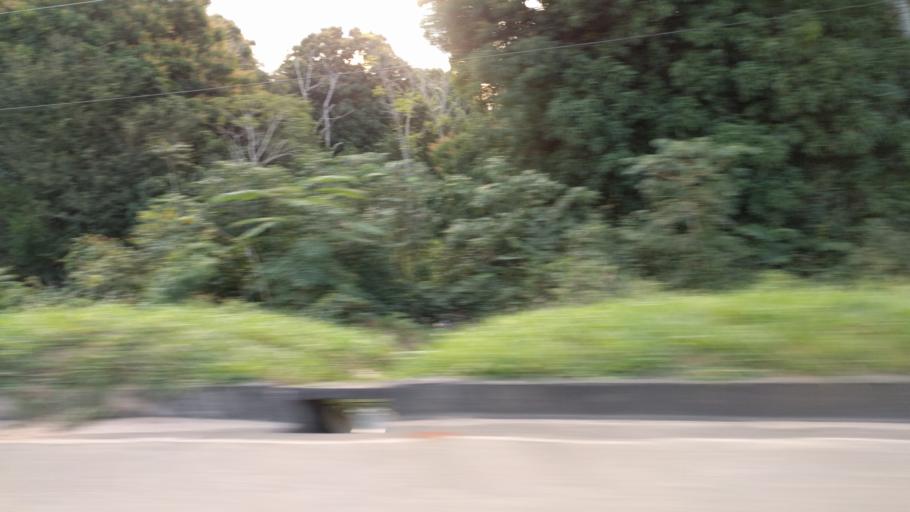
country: BO
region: Santa Cruz
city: Buena Vista
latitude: -17.4501
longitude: -63.6516
